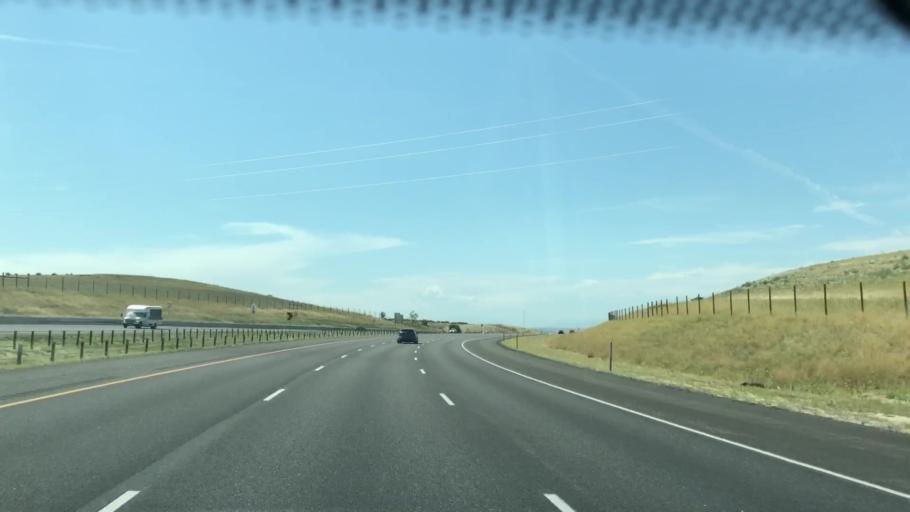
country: US
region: Colorado
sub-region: Douglas County
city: Parker
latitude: 39.5704
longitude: -104.7538
